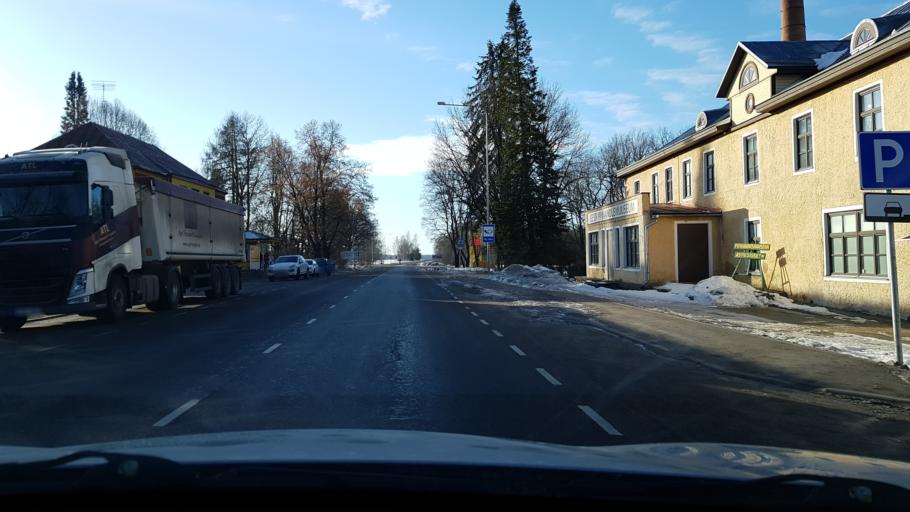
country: EE
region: Jogevamaa
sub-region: Poltsamaa linn
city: Poltsamaa
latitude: 58.7338
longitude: 25.7670
